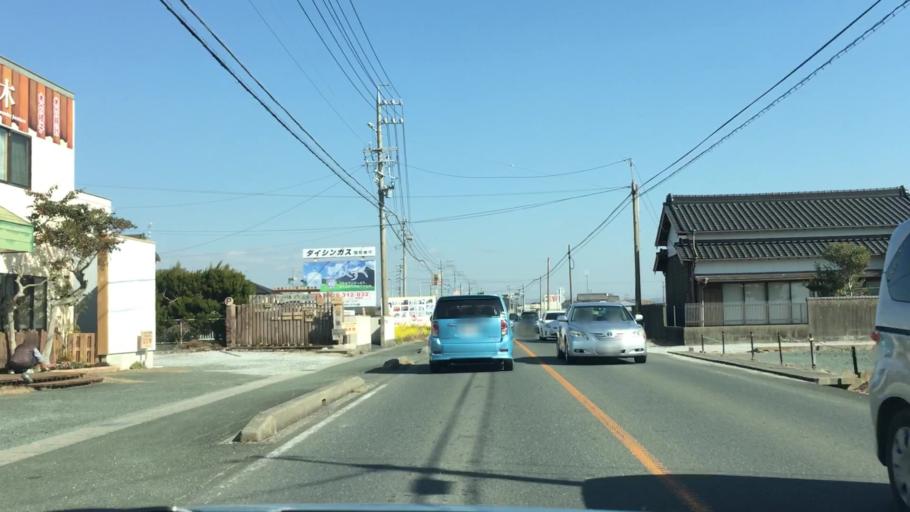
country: JP
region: Aichi
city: Tahara
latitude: 34.6874
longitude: 137.3219
